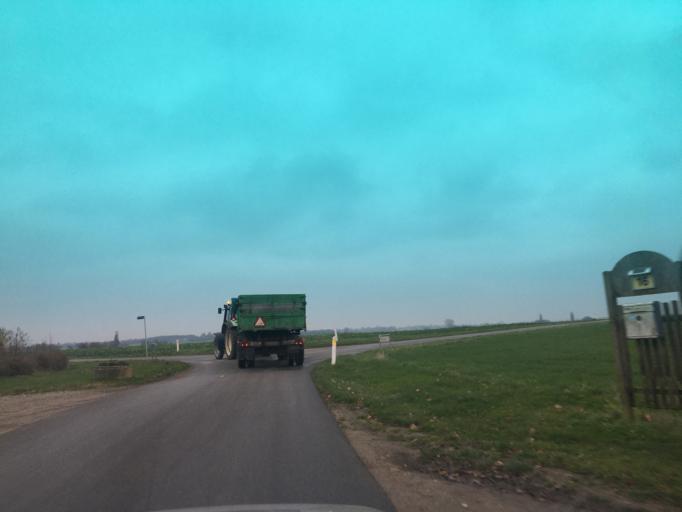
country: DK
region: Zealand
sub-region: Slagelse Kommune
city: Skaelskor
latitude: 55.2654
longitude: 11.4190
